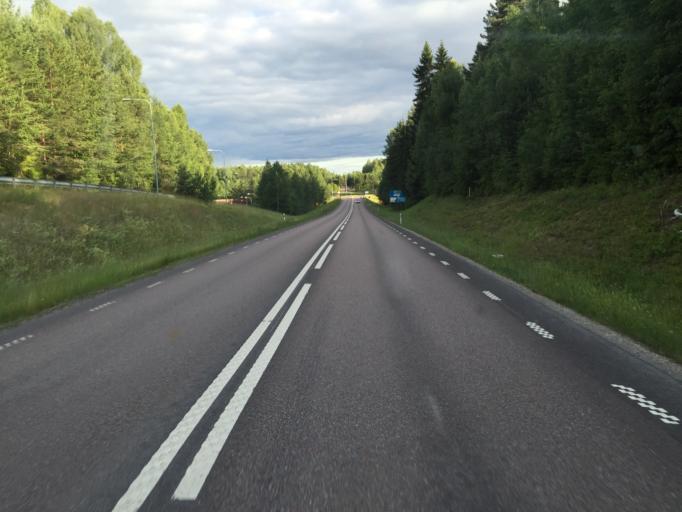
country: SE
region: Dalarna
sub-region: Borlange Kommun
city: Borlaenge
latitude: 60.5091
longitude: 15.3842
